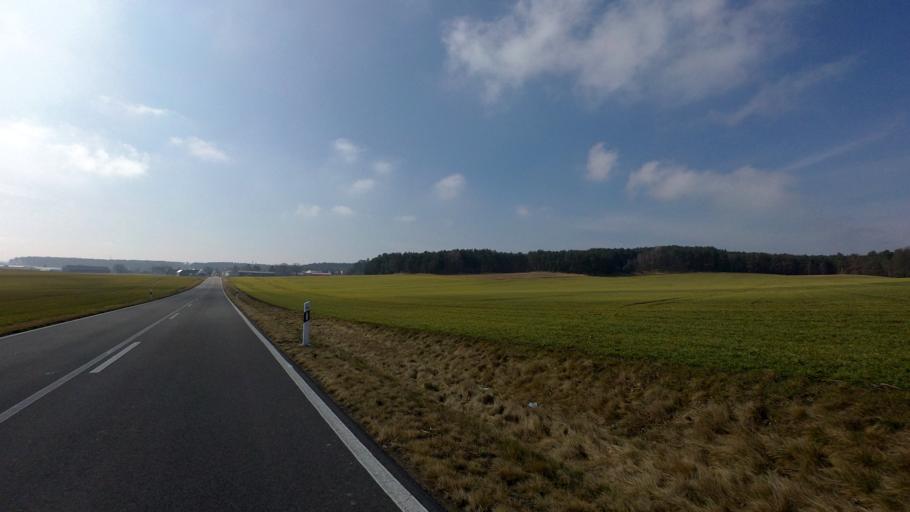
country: DE
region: Brandenburg
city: Belzig
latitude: 52.1064
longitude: 12.6202
